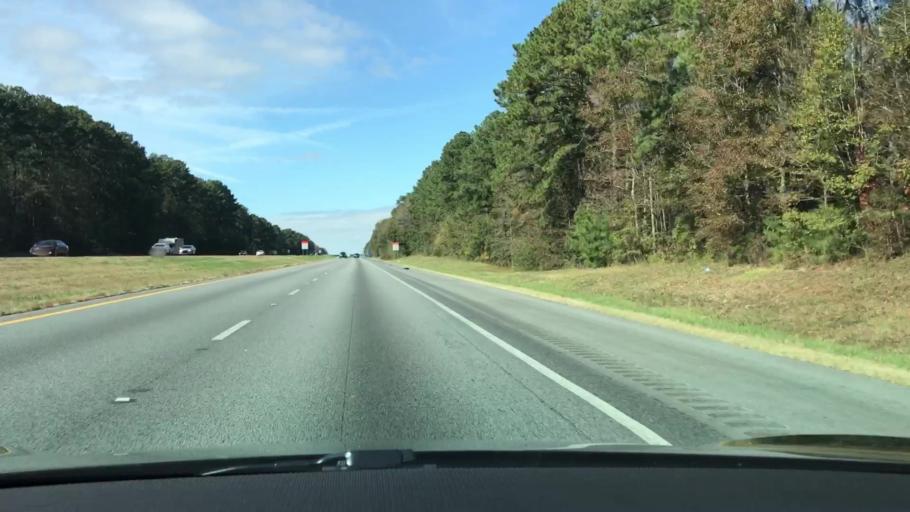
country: US
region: Georgia
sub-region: Morgan County
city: Madison
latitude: 33.5840
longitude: -83.5989
